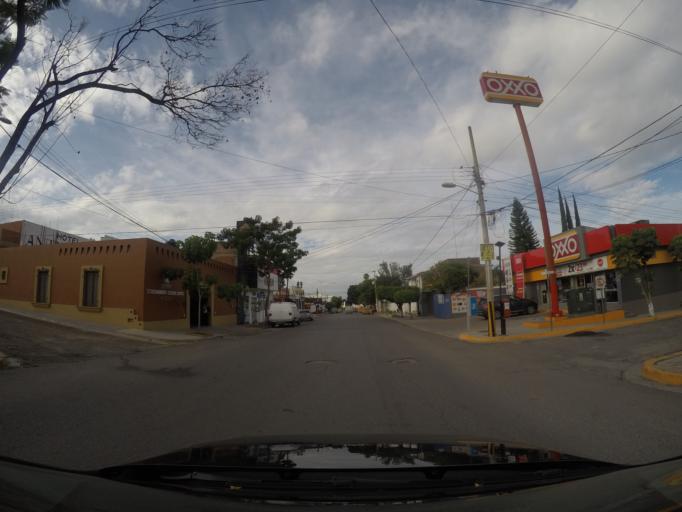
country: MX
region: Oaxaca
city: Oaxaca de Juarez
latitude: 17.0723
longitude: -96.7165
